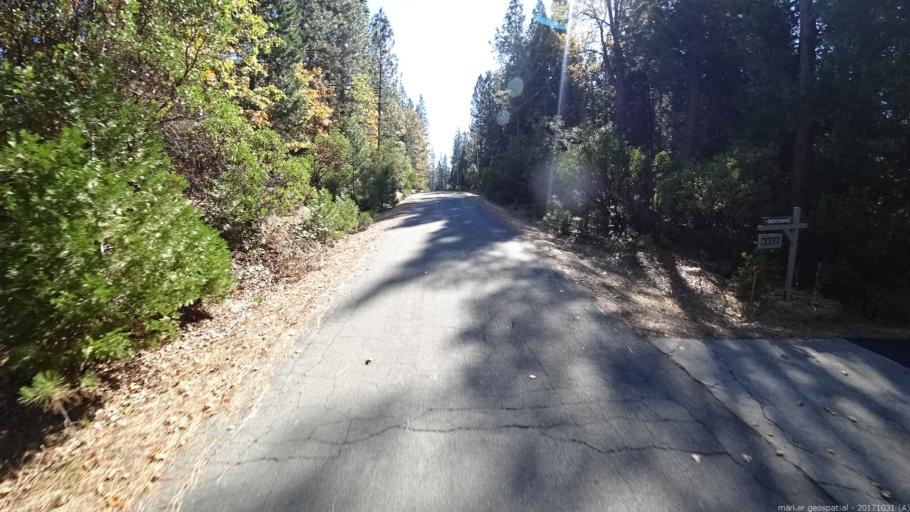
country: US
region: California
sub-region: Shasta County
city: Shingletown
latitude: 40.4861
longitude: -121.8863
